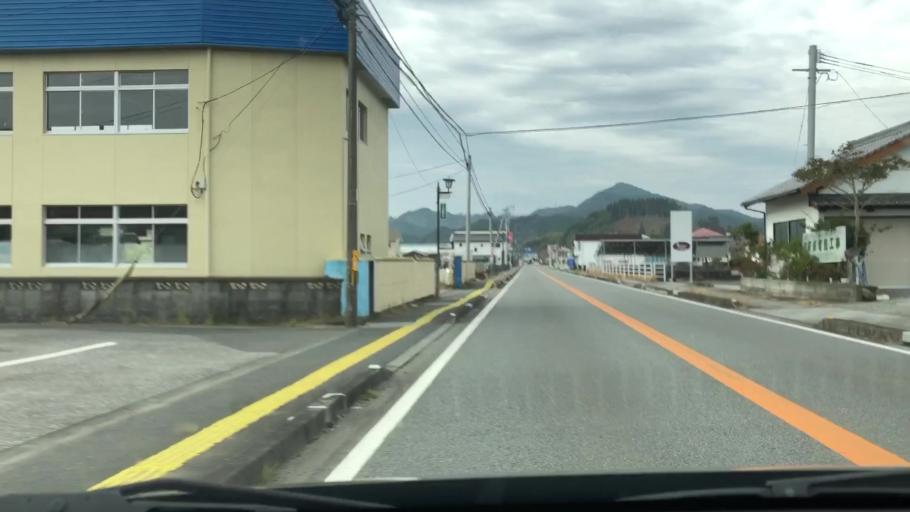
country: JP
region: Oita
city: Saiki
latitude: 32.9739
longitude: 131.8426
